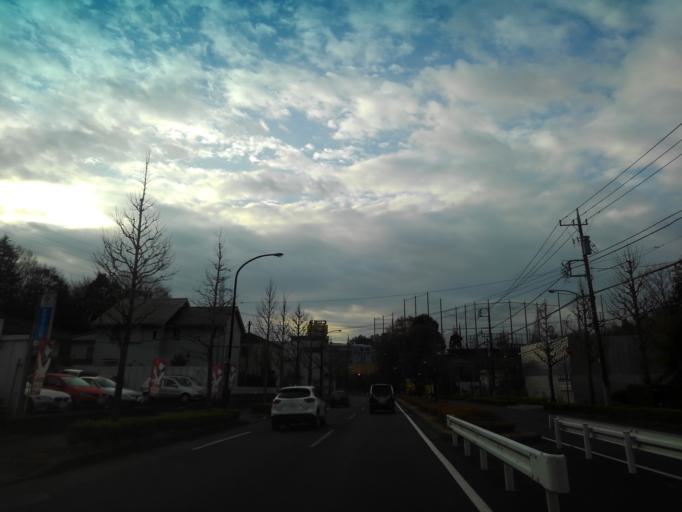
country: JP
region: Tokyo
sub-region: Machida-shi
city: Machida
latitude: 35.6007
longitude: 139.4457
